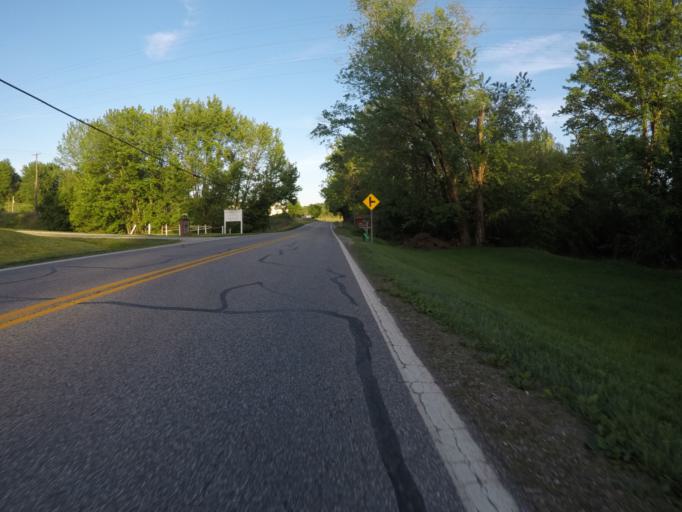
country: US
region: West Virginia
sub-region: Cabell County
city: Huntington
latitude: 38.4876
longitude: -82.4713
